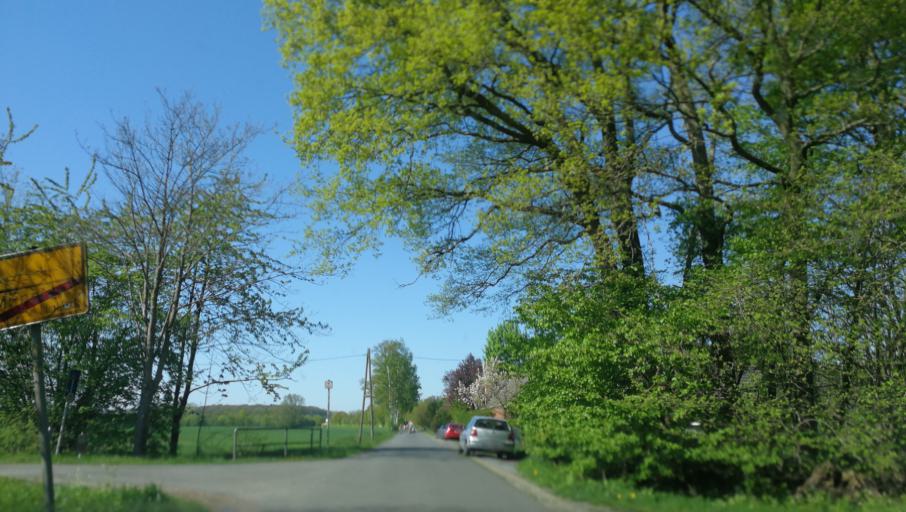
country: DE
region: North Rhine-Westphalia
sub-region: Regierungsbezirk Munster
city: Muenster
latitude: 51.9308
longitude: 7.5597
